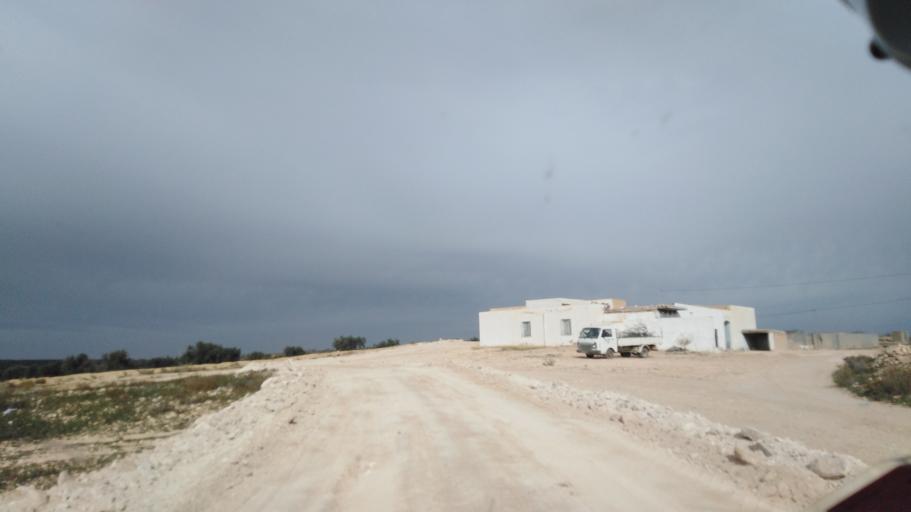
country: TN
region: Safaqis
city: Bi'r `Ali Bin Khalifah
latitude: 34.8149
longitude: 10.3074
